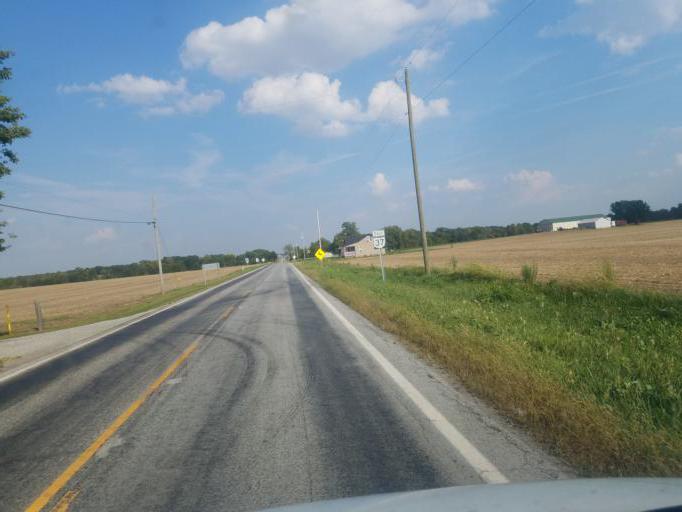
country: US
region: Ohio
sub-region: Hancock County
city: Arlington
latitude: 40.8910
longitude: -83.5557
